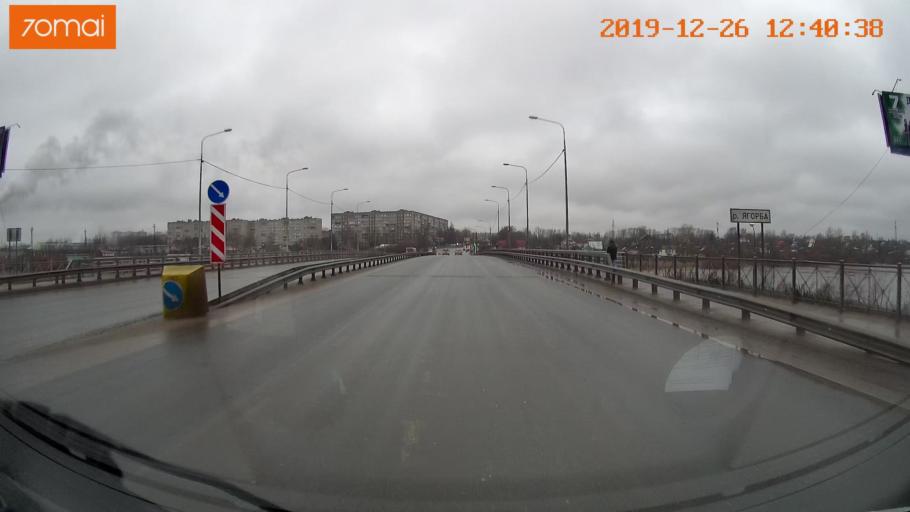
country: RU
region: Vologda
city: Tonshalovo
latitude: 59.1429
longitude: 37.9702
